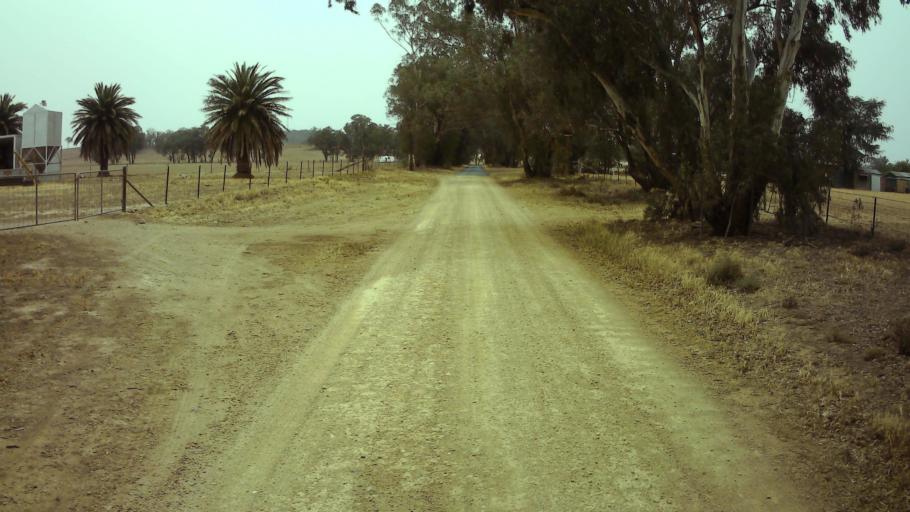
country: AU
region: New South Wales
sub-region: Weddin
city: Grenfell
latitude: -33.8995
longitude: 148.1426
